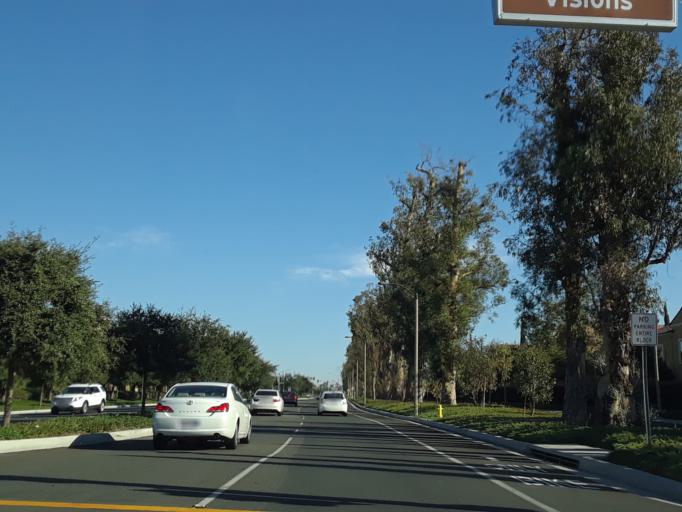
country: US
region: California
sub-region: Orange County
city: Irvine
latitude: 33.6915
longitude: -117.7616
